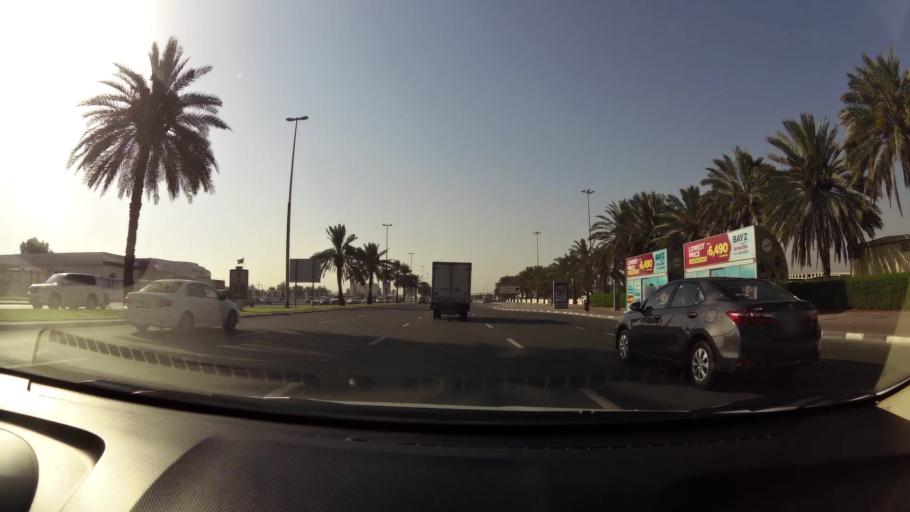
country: AE
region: Ash Shariqah
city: Sharjah
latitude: 25.2711
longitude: 55.3525
